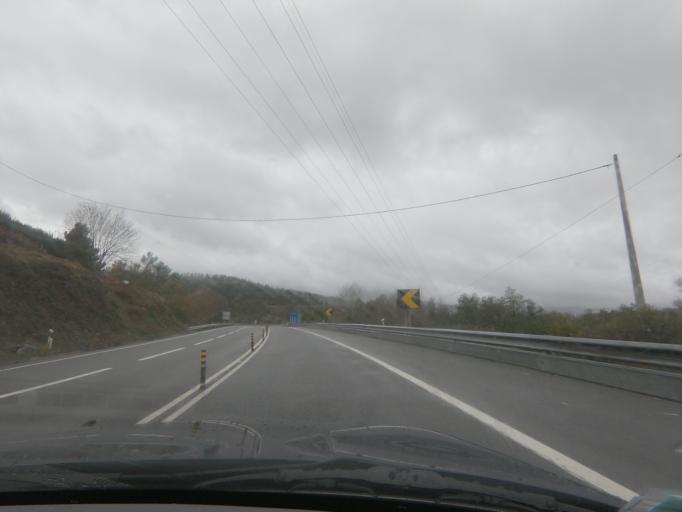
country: PT
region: Vila Real
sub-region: Santa Marta de Penaguiao
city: Santa Marta de Penaguiao
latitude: 41.2849
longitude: -7.8314
